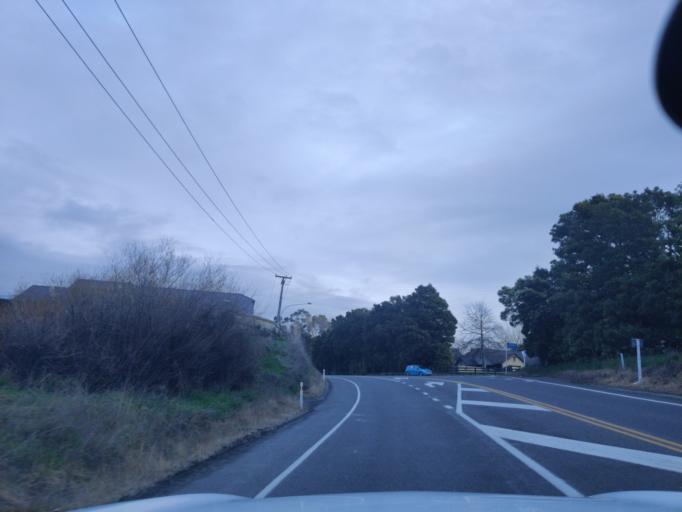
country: NZ
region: Manawatu-Wanganui
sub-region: Palmerston North City
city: Palmerston North
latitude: -40.3810
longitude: 175.6472
